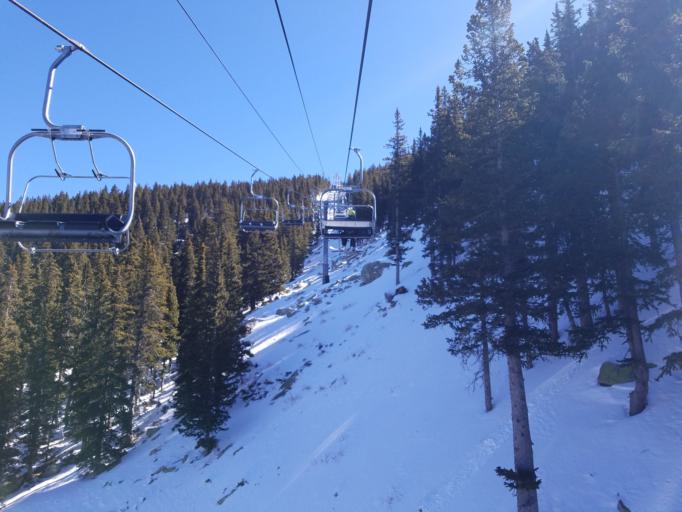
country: US
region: New Mexico
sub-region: Santa Fe County
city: Santa Fe
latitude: 35.7923
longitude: -105.7817
